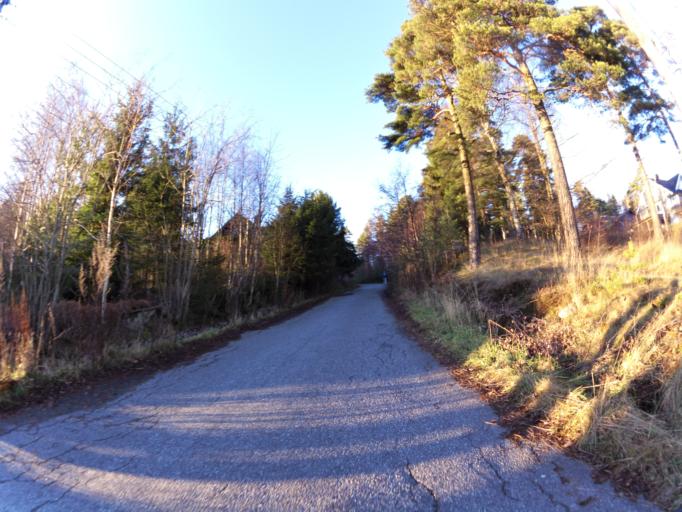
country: NO
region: Ostfold
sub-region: Fredrikstad
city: Fredrikstad
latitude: 59.2406
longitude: 10.9662
